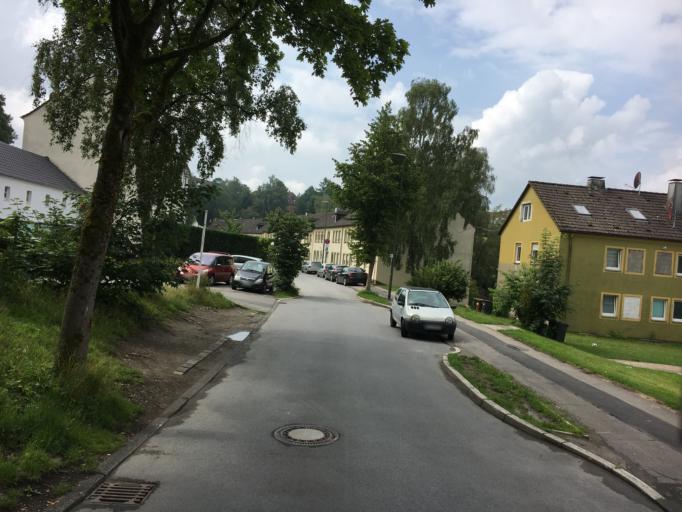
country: DE
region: North Rhine-Westphalia
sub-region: Regierungsbezirk Arnsberg
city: Luedenscheid
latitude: 51.2258
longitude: 7.6400
